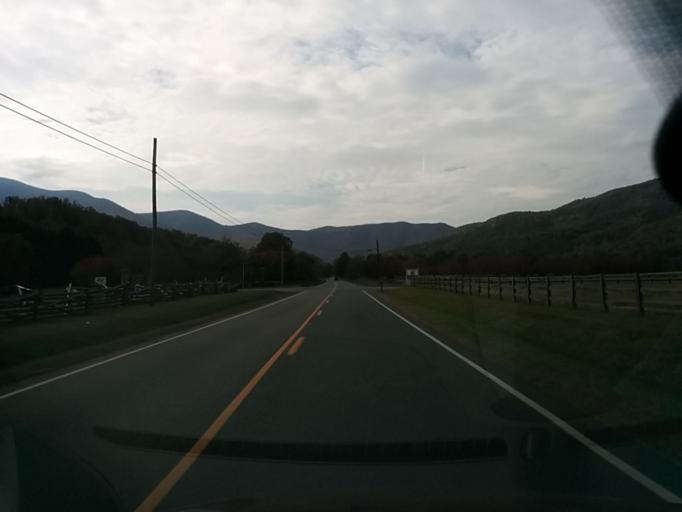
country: US
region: Virginia
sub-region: Nelson County
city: Nellysford
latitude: 37.8726
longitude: -78.9234
